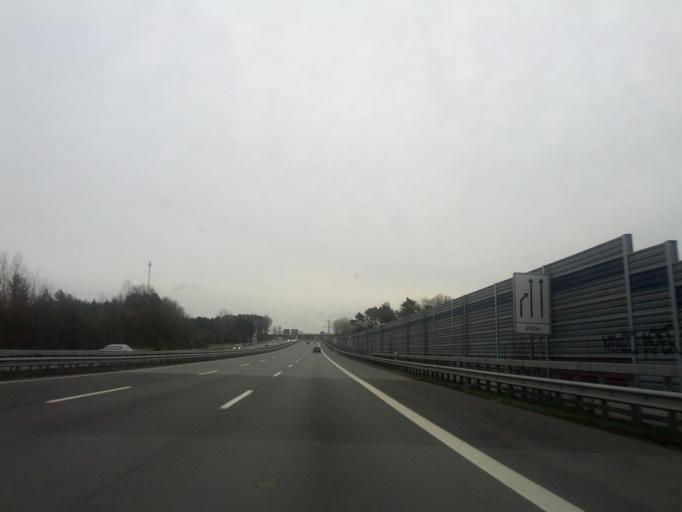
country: DE
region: Lower Saxony
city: Buchholz in der Nordheide
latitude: 53.3727
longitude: 9.8548
